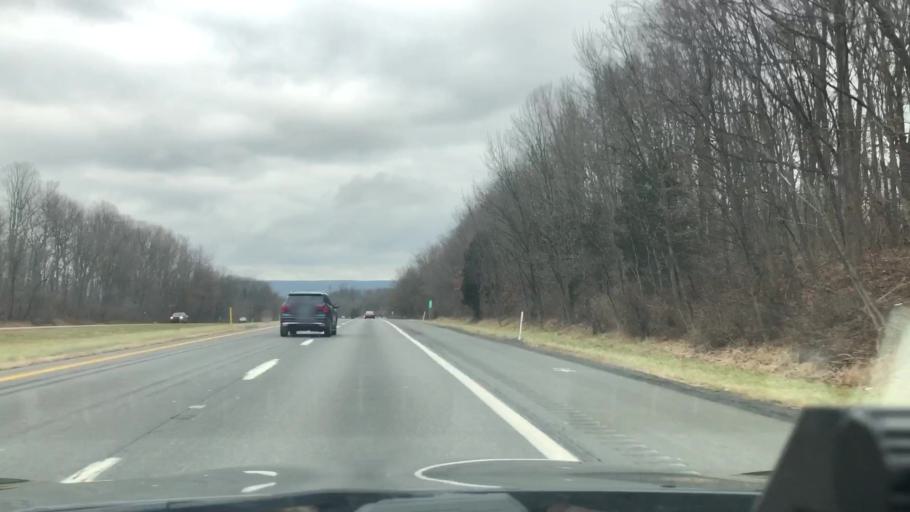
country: US
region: Pennsylvania
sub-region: Northampton County
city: Belfast
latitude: 40.7889
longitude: -75.2877
